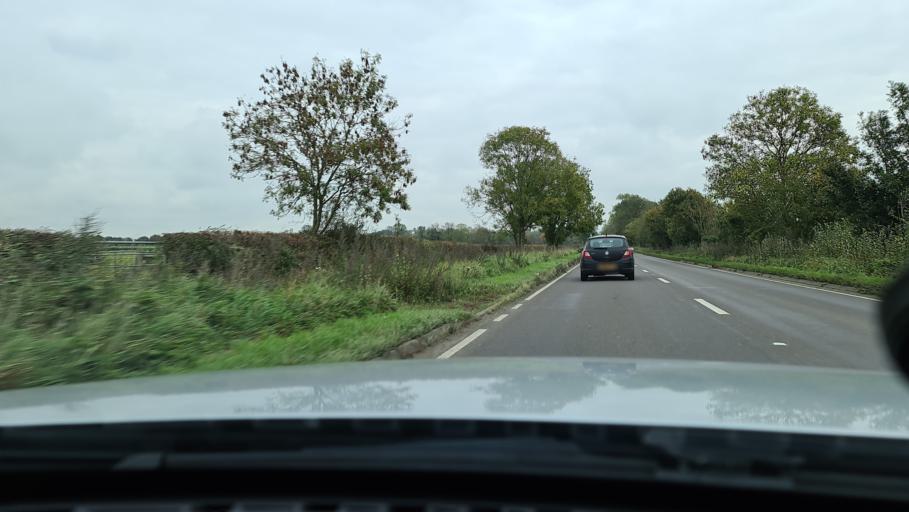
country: GB
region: England
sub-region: Oxfordshire
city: Bicester
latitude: 51.8781
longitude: -1.1063
